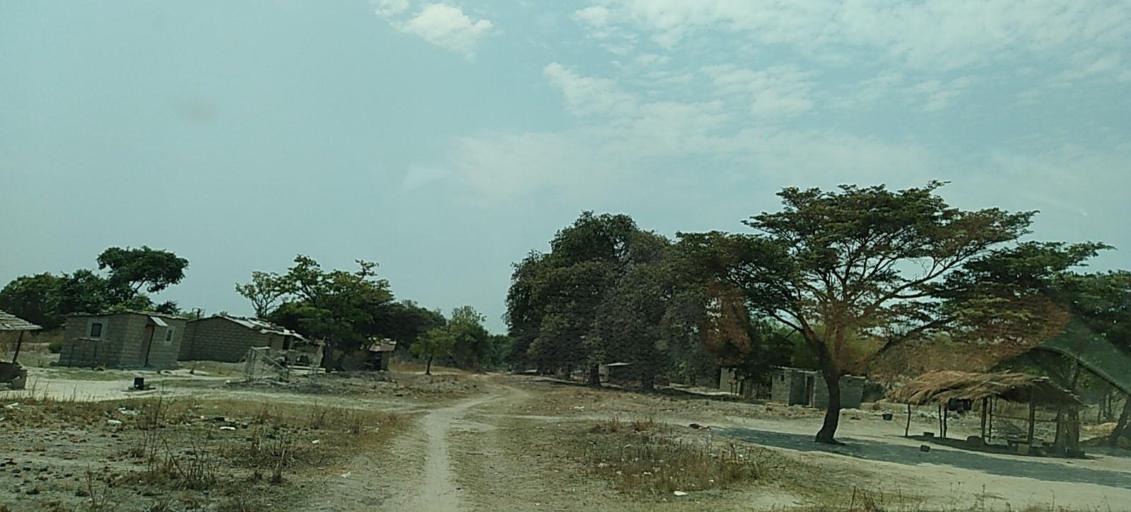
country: ZM
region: Copperbelt
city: Kalulushi
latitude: -12.9446
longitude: 28.1248
